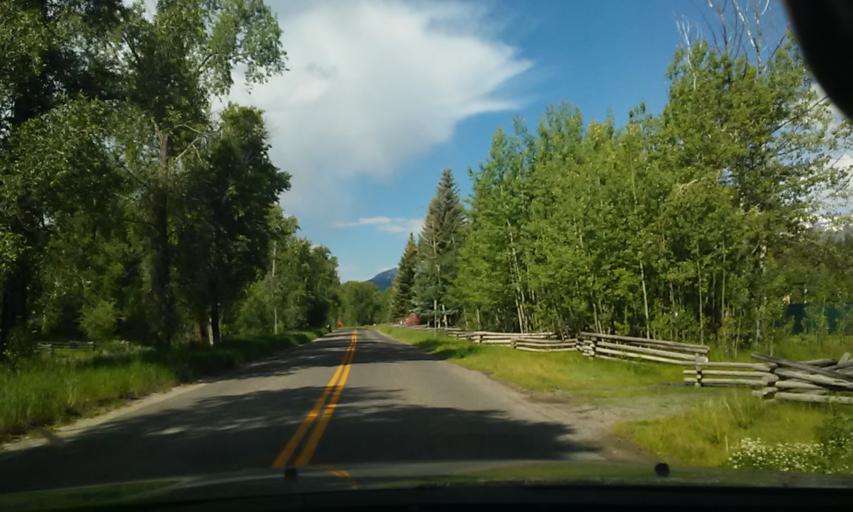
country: US
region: Wyoming
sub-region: Teton County
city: Jackson
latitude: 43.5634
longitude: -110.7519
